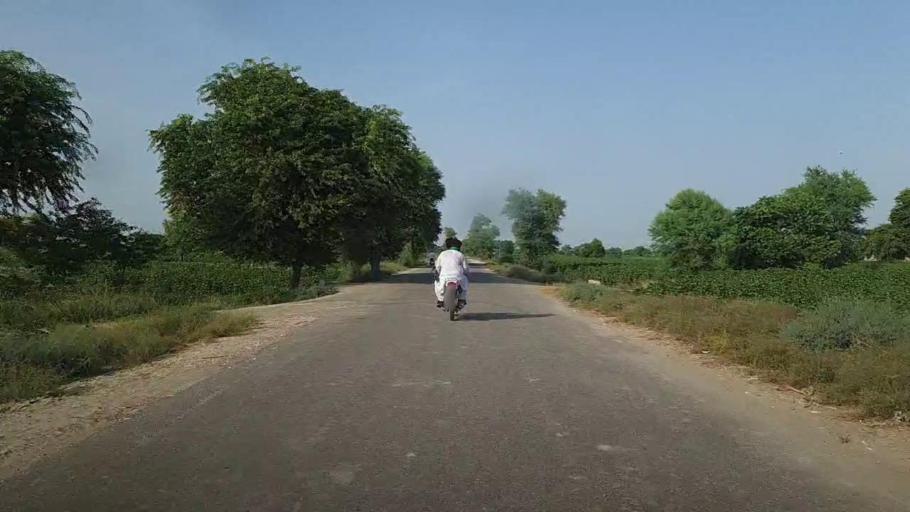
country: PK
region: Sindh
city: Khairpur
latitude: 28.0765
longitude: 69.8302
